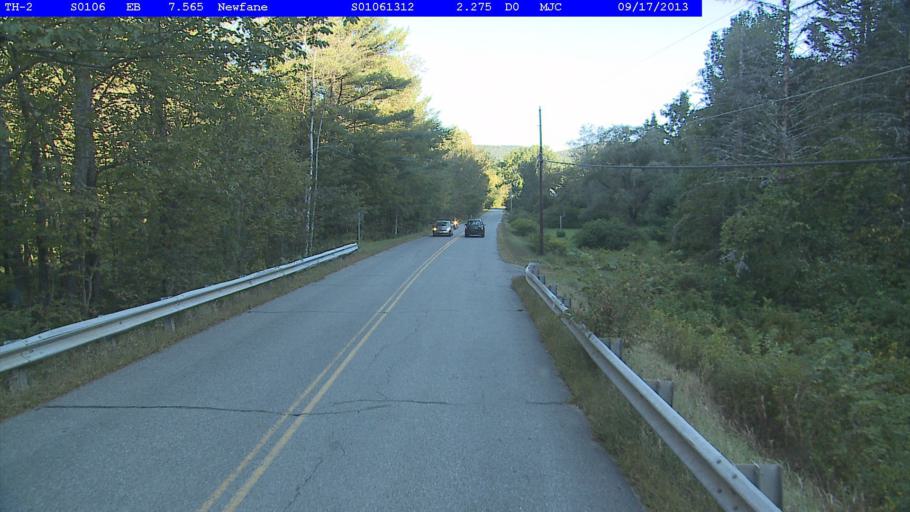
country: US
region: Vermont
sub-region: Windham County
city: Dover
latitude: 42.9439
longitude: -72.7267
